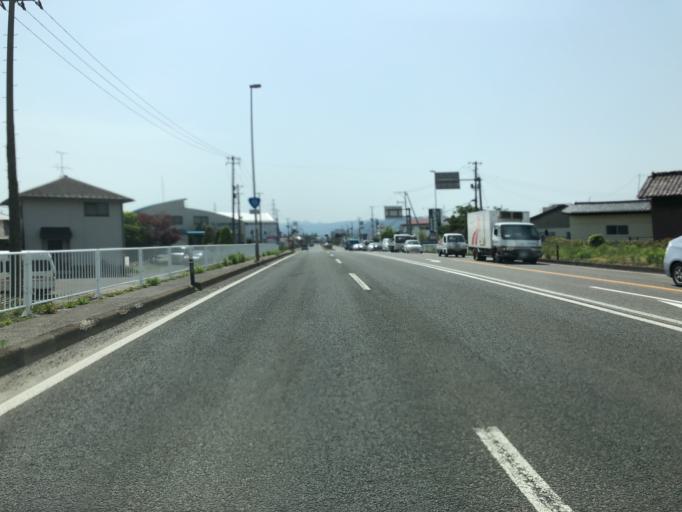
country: JP
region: Fukushima
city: Fukushima-shi
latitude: 37.8108
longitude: 140.4449
